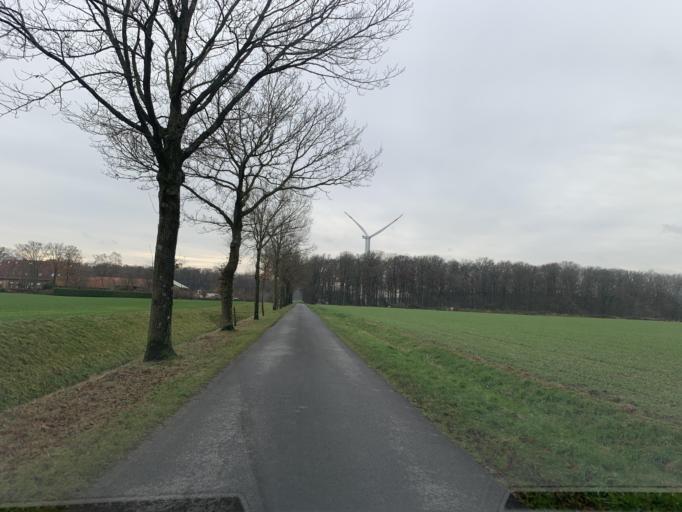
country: DE
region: North Rhine-Westphalia
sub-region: Regierungsbezirk Munster
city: Senden
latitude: 51.8893
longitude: 7.5429
